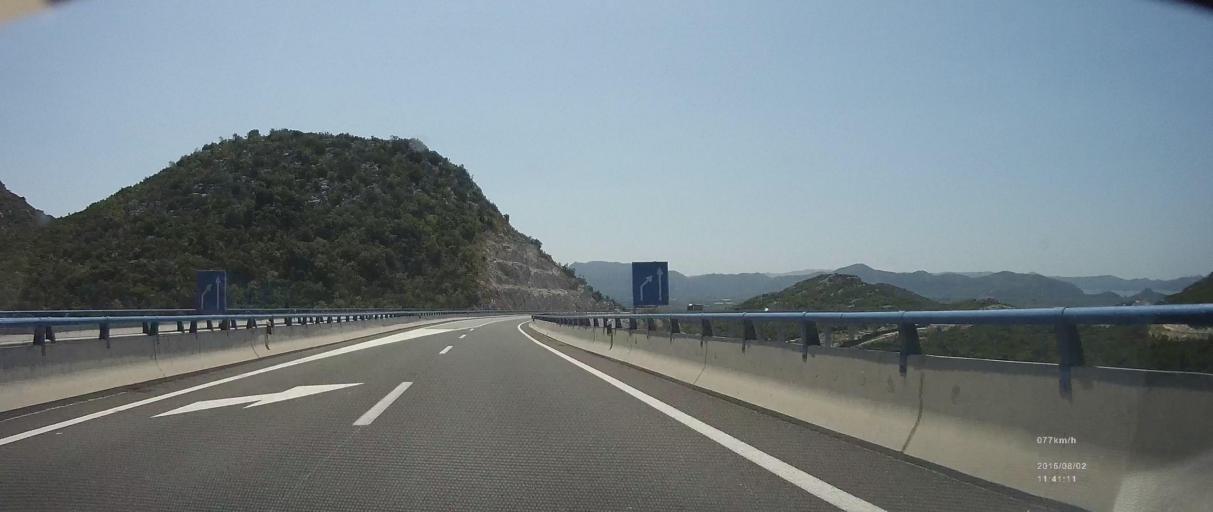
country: HR
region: Dubrovacko-Neretvanska
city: Komin
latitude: 43.0662
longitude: 17.4945
